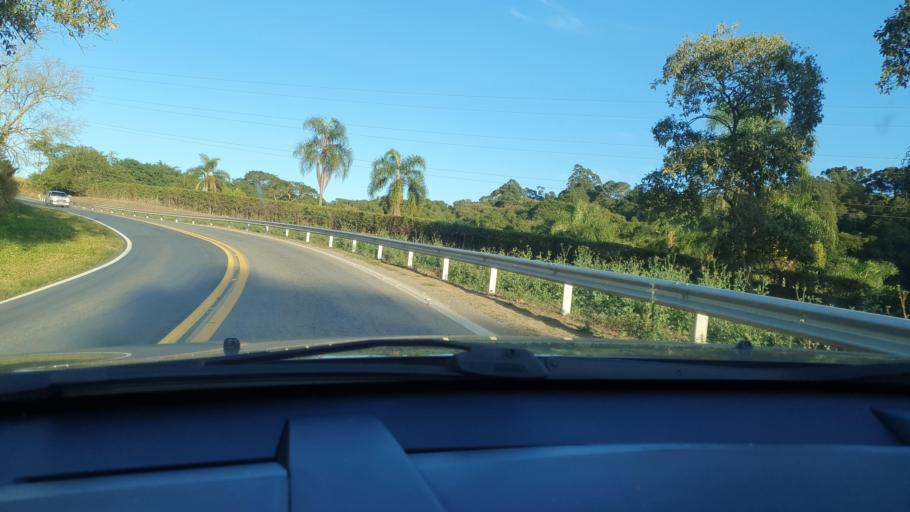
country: BR
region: Sao Paulo
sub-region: Piedade
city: Piedade
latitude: -23.6767
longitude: -47.3272
